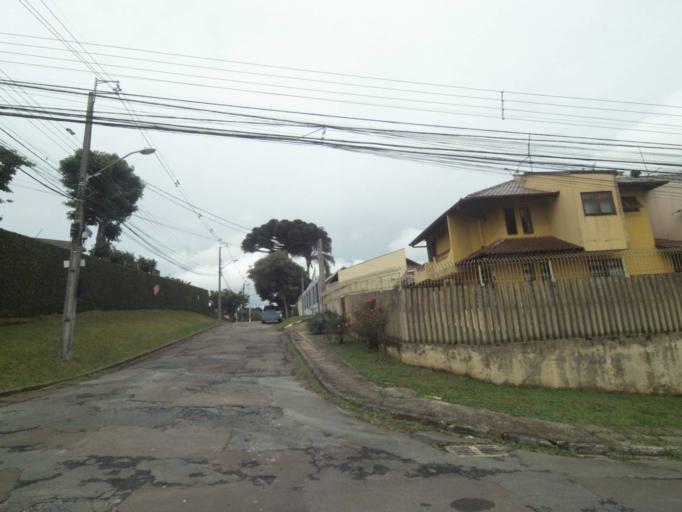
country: BR
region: Parana
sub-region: Curitiba
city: Curitiba
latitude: -25.4466
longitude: -49.3439
